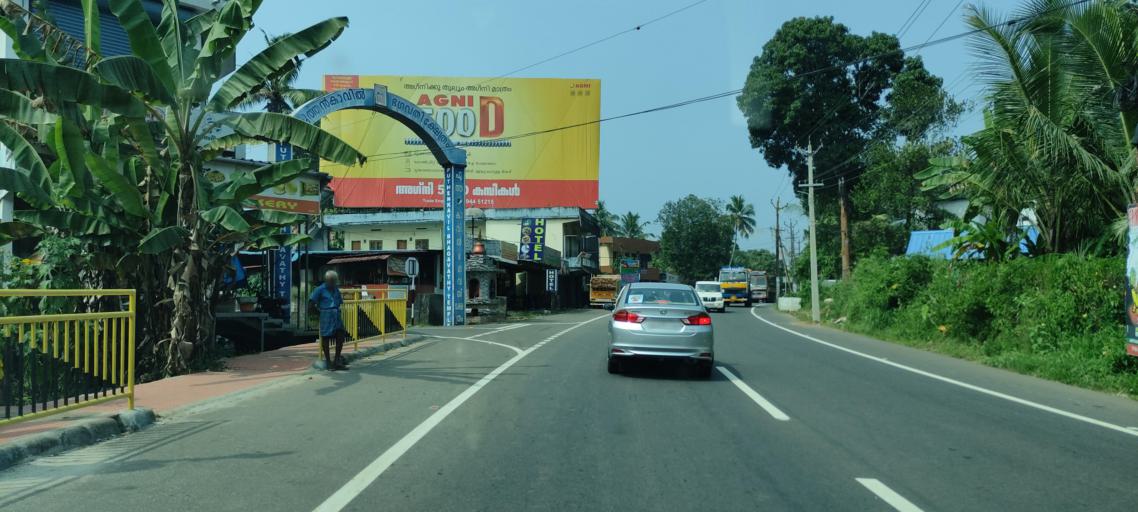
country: IN
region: Kerala
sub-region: Pattanamtitta
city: Adur
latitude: 9.1998
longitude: 76.6946
